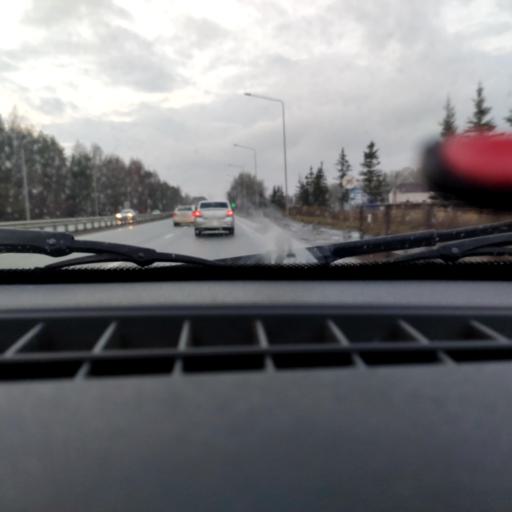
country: RU
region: Bashkortostan
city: Ufa
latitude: 54.5616
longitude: 55.9227
